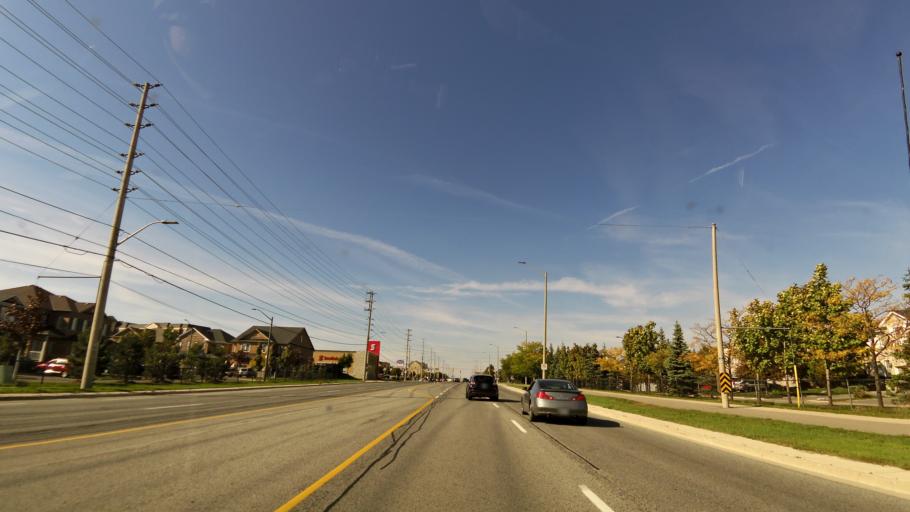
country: CA
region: Ontario
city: Mississauga
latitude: 43.5593
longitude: -79.7314
